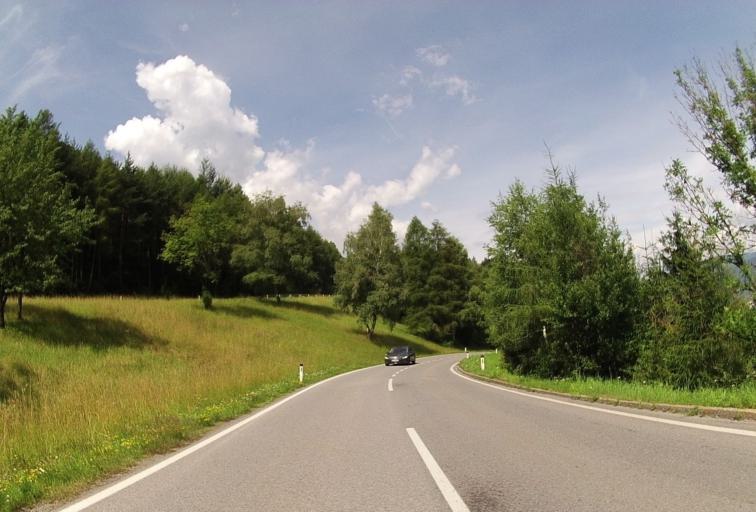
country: AT
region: Tyrol
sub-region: Politischer Bezirk Innsbruck Land
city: Kematen in Tirol
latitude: 47.2480
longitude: 11.2781
